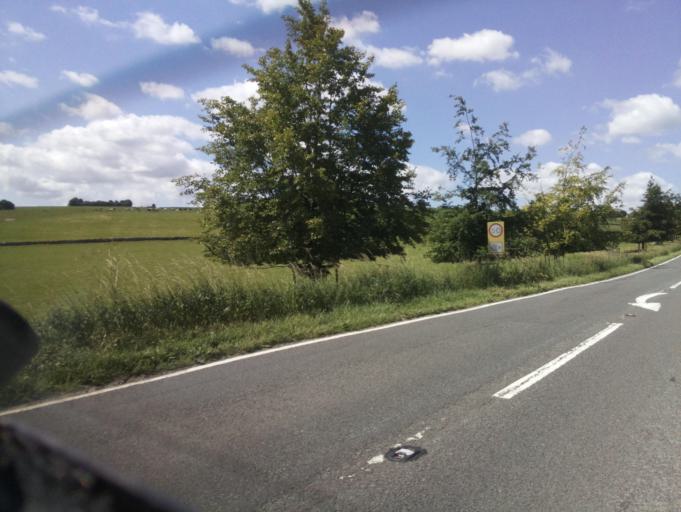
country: GB
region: England
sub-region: Derbyshire
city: Ashbourne
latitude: 53.0723
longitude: -1.7522
